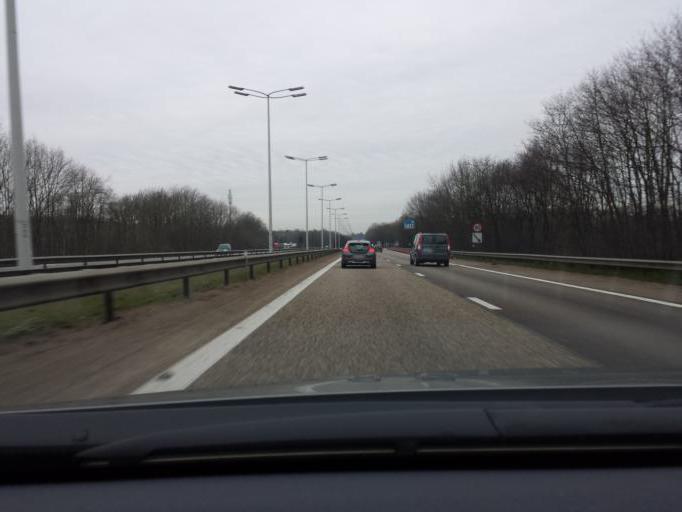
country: BE
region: Flanders
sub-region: Provincie Limburg
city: Zonhoven
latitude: 51.0123
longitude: 5.3401
